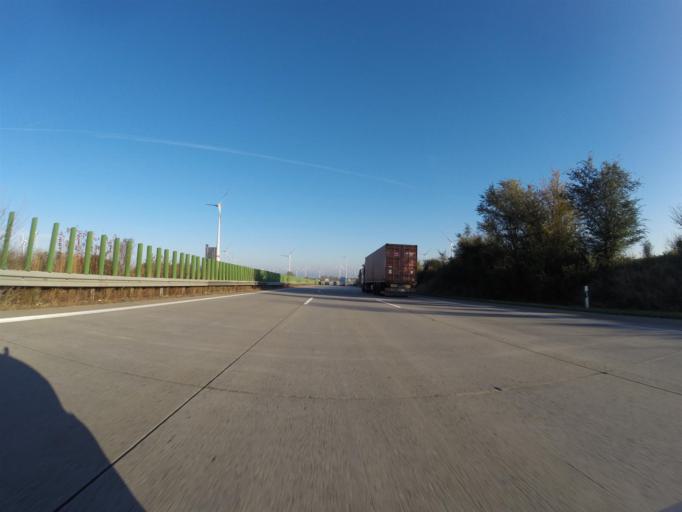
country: DE
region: Saxony-Anhalt
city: Stossen
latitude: 51.1219
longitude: 11.9574
